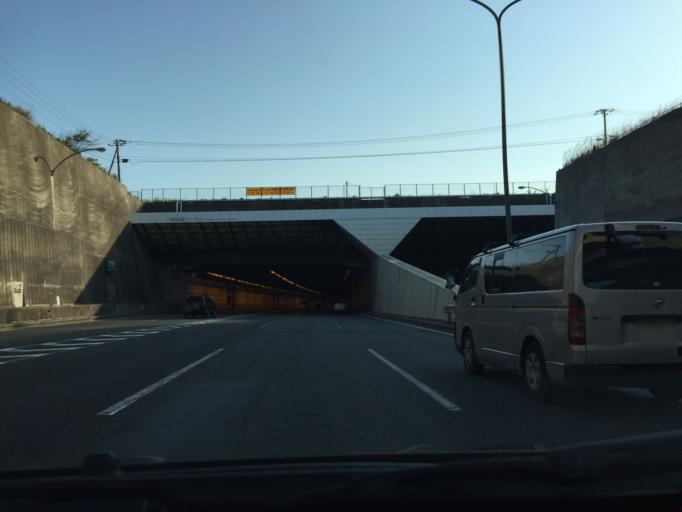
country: JP
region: Kanagawa
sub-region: Kawasaki-shi
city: Kawasaki
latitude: 35.5135
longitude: 139.7879
